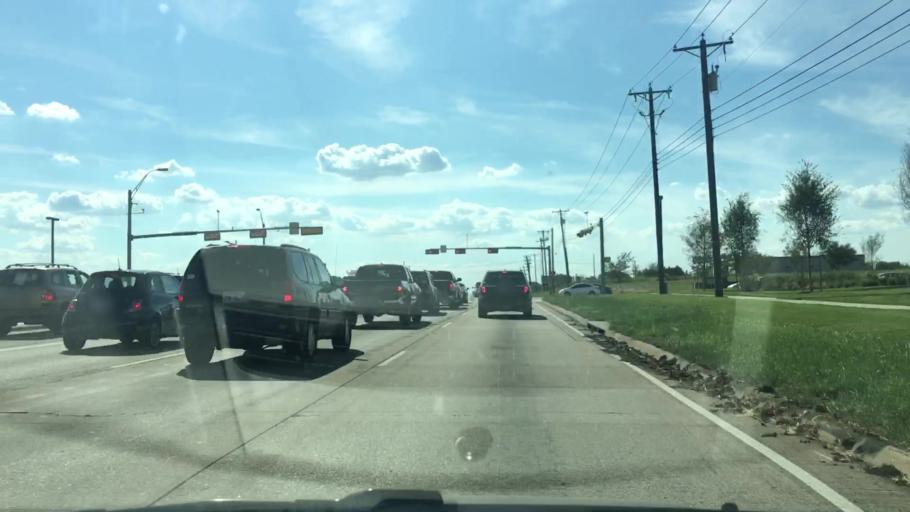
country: US
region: Texas
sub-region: Collin County
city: McKinney
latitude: 33.2174
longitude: -96.6604
